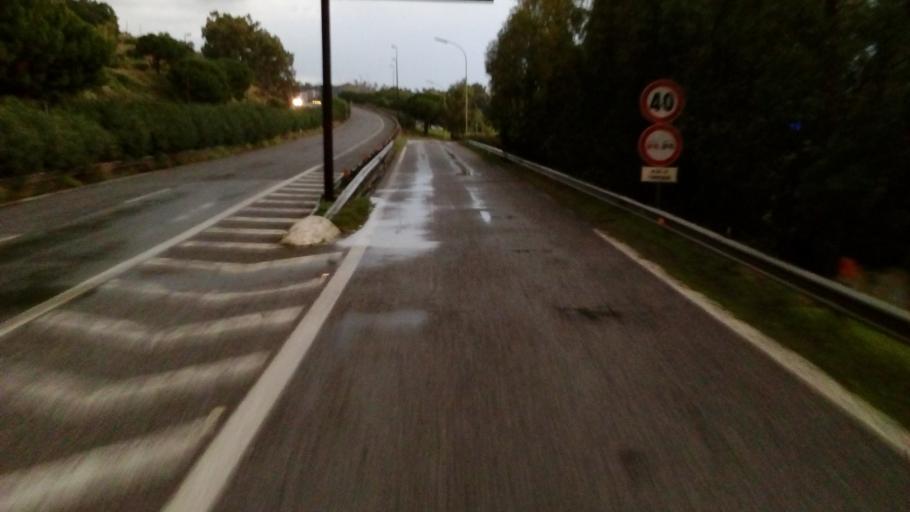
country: IT
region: Sicily
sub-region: Messina
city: Larderia
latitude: 38.1307
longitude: 15.5195
